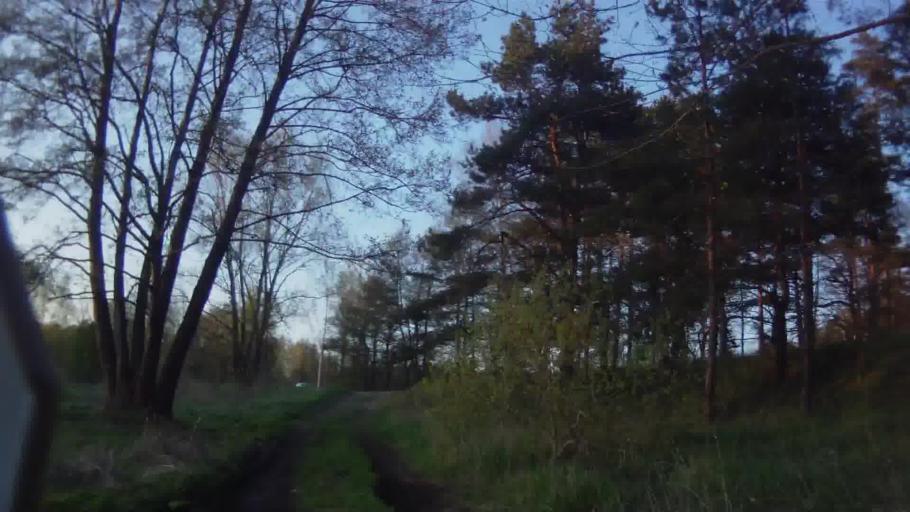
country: LV
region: Riga
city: Jaunciems
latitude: 57.0136
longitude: 24.2118
